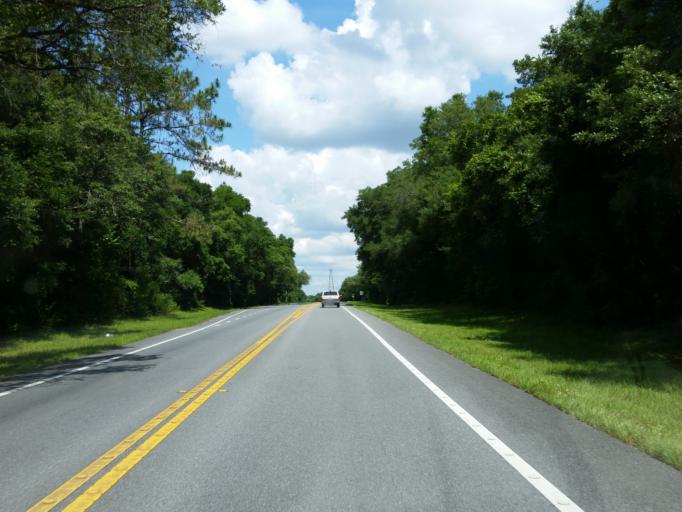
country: US
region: Florida
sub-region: Citrus County
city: Citrus Springs
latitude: 28.9953
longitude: -82.4418
